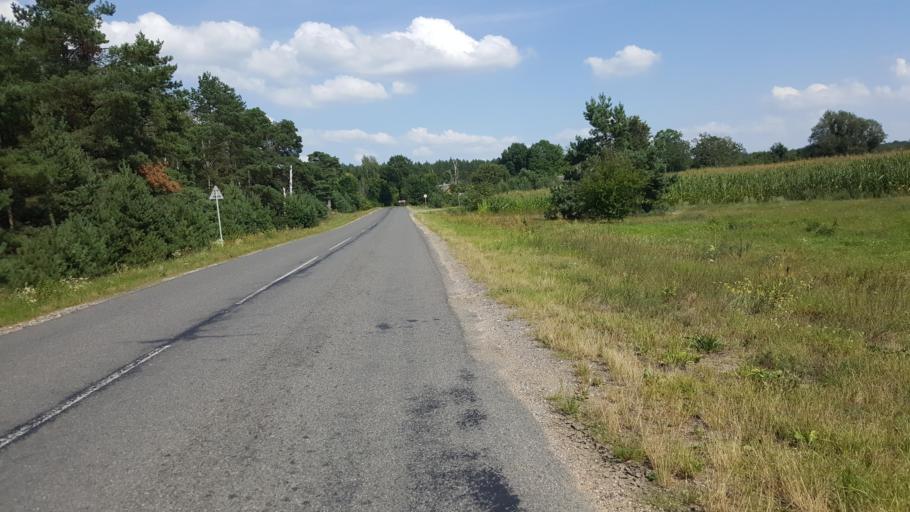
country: BY
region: Brest
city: Kamyanyuki
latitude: 52.5055
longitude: 23.6486
